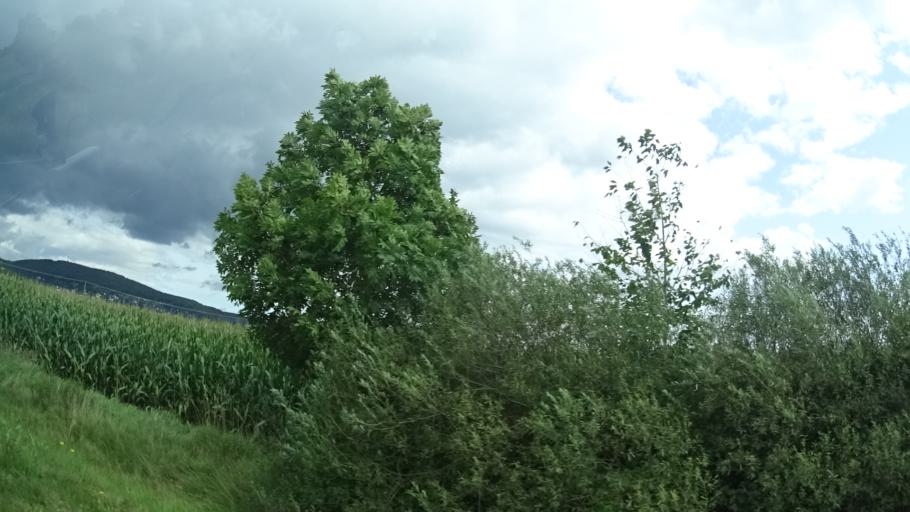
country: DE
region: Bavaria
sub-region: Upper Franconia
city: Ebersdorf
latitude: 50.3418
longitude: 11.1652
